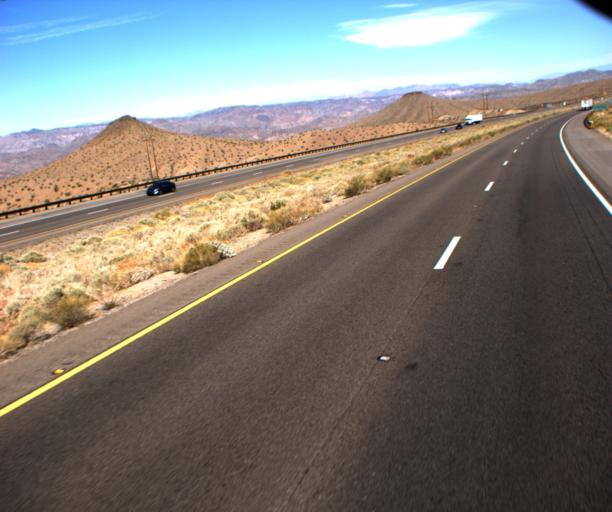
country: US
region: Nevada
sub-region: Clark County
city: Boulder City
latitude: 35.8604
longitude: -114.5996
